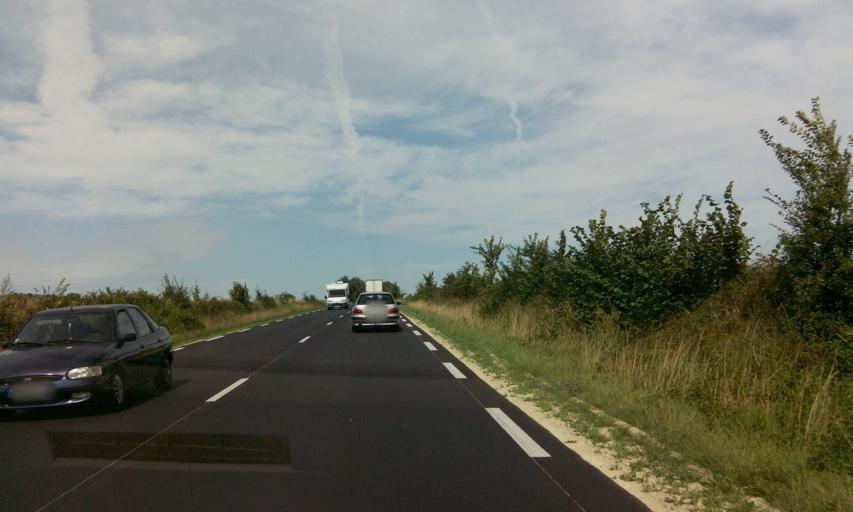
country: FR
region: Poitou-Charentes
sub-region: Departement des Deux-Sevres
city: Sauze-Vaussais
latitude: 46.1420
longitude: 0.0880
